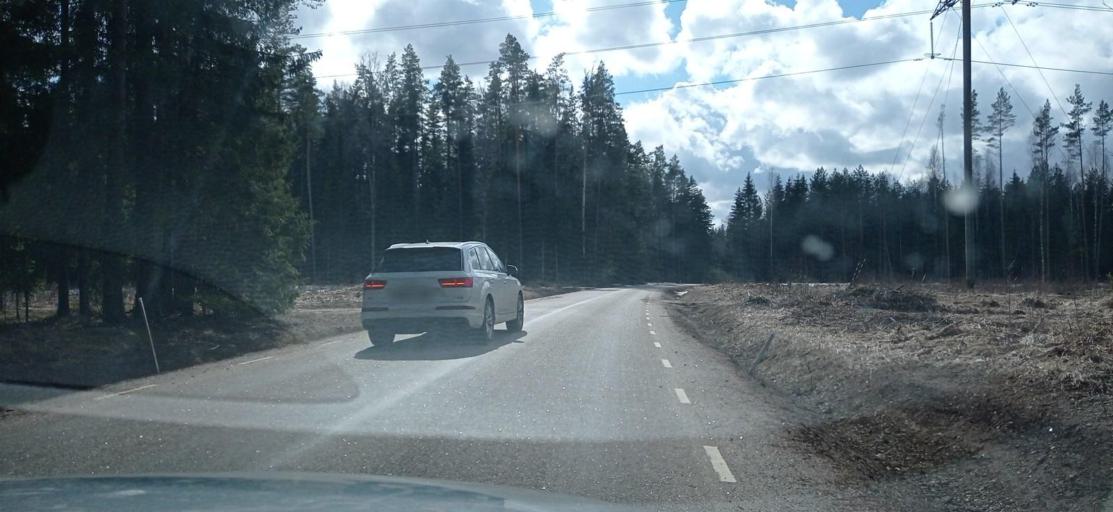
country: EE
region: Polvamaa
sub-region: Polva linn
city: Polva
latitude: 58.1475
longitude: 27.0394
